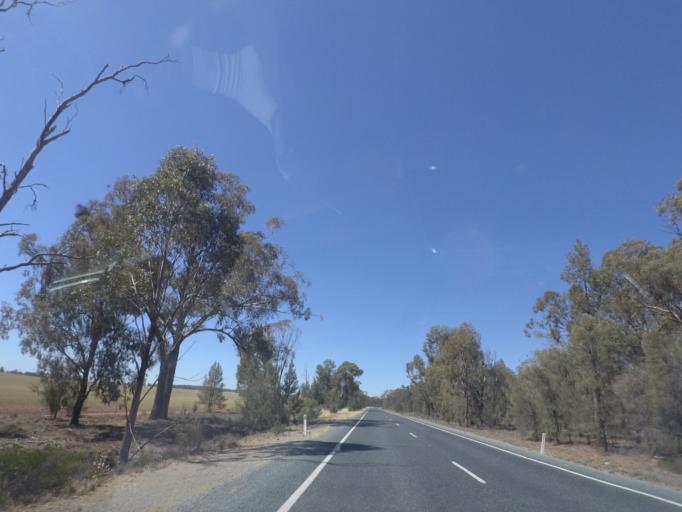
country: AU
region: New South Wales
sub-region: Narrandera
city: Narrandera
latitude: -34.4367
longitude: 146.8421
